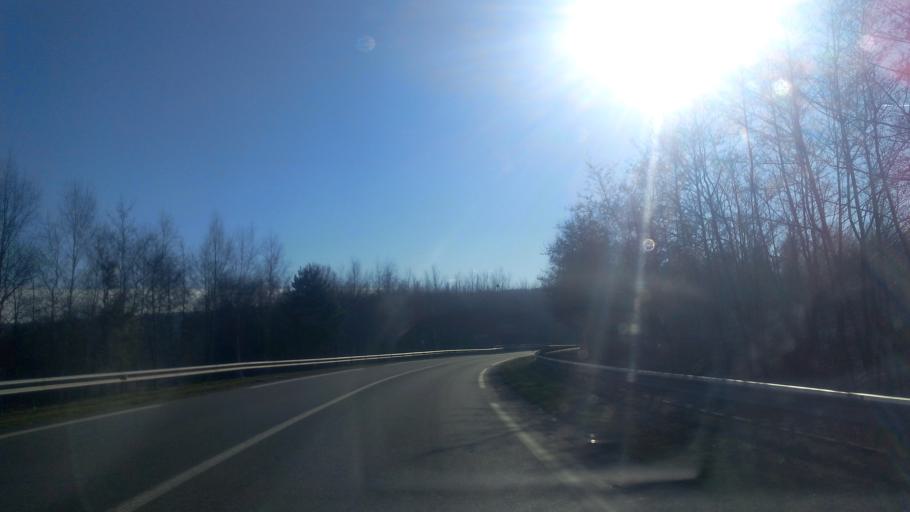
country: FR
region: Brittany
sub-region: Departement du Morbihan
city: La Gacilly
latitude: 47.7722
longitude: -2.1218
